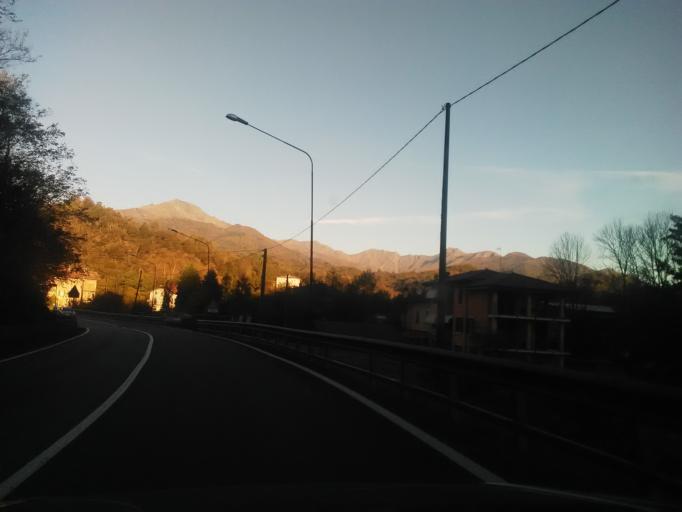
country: IT
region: Piedmont
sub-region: Provincia di Biella
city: Crevacuore
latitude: 45.6806
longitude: 8.2507
